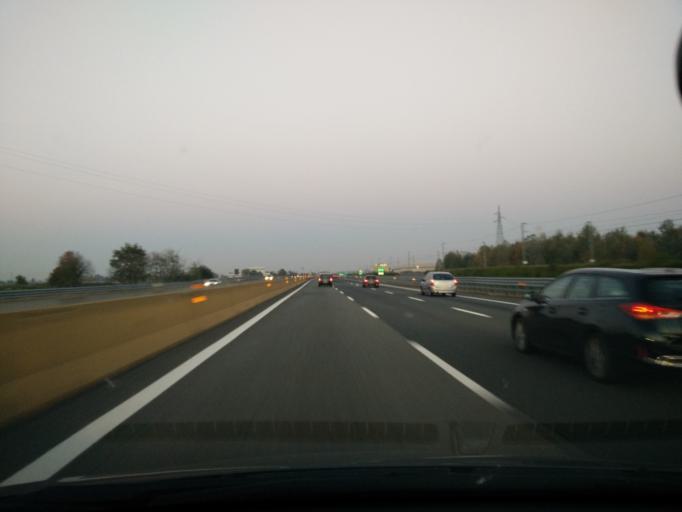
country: IT
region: Piedmont
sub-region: Provincia di Vercelli
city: Carisio
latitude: 45.4306
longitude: 8.2043
